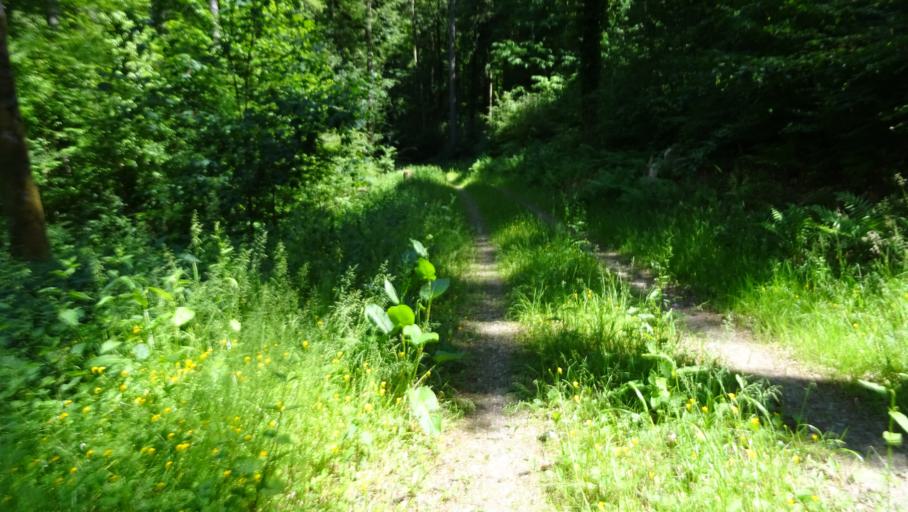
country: DE
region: Baden-Wuerttemberg
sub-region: Karlsruhe Region
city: Binau
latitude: 49.3309
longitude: 9.0526
